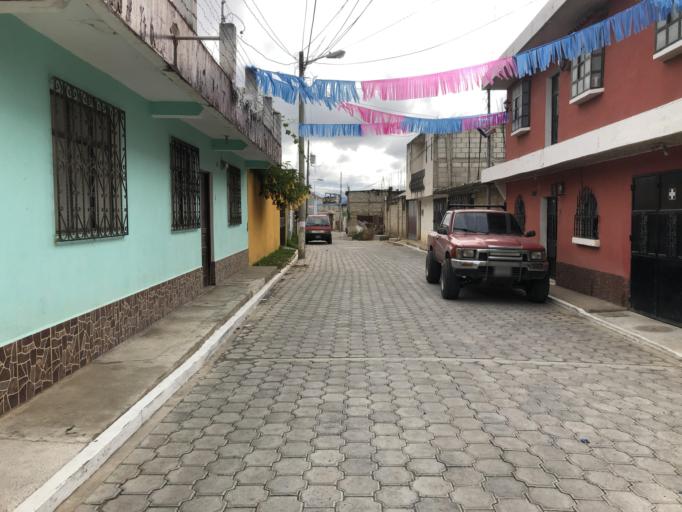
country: GT
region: Quetzaltenango
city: Quetzaltenango
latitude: 14.8392
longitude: -91.5372
